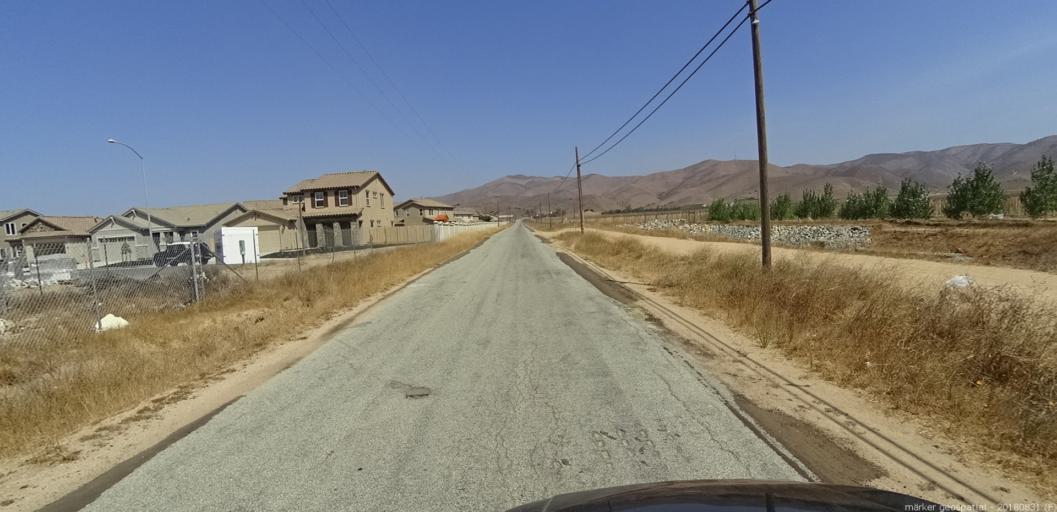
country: US
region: California
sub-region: Monterey County
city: Soledad
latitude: 36.4367
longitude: -121.3118
